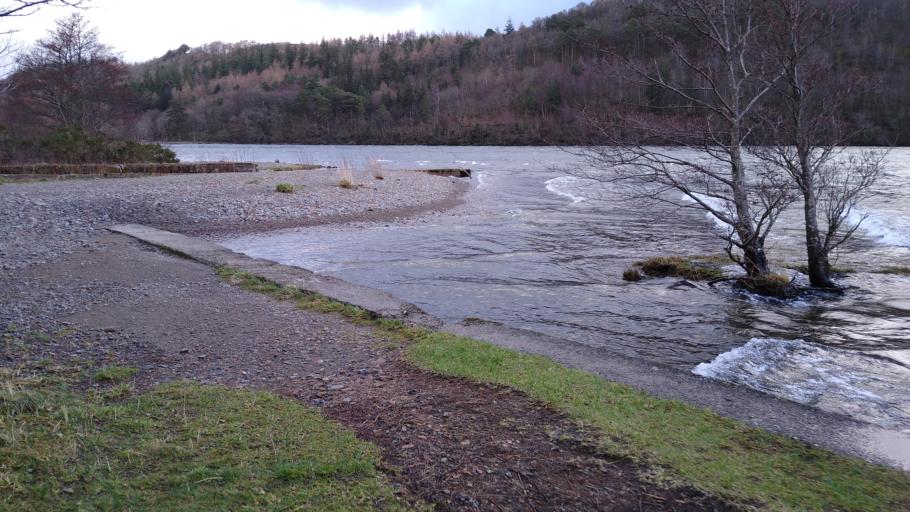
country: GB
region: England
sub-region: Cumbria
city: Cockermouth
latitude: 54.5729
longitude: -3.3138
